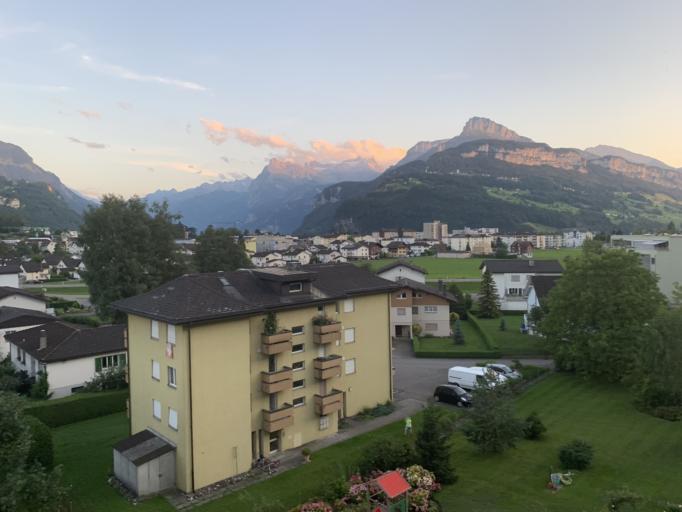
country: CH
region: Schwyz
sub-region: Bezirk Schwyz
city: Ingenbohl
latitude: 47.0023
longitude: 8.6042
